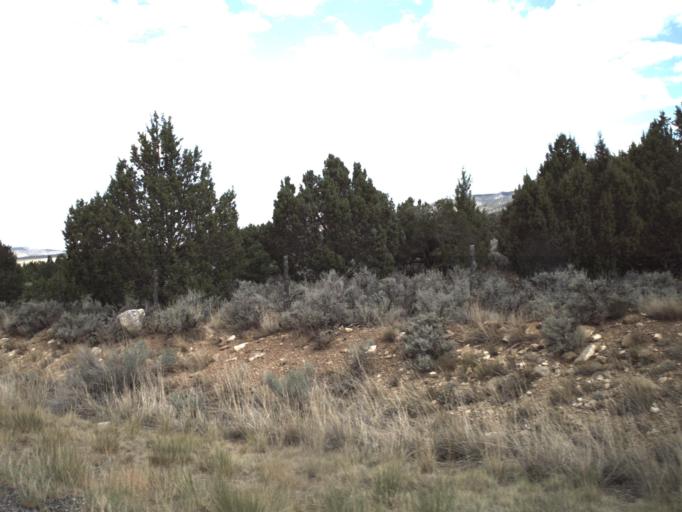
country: US
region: Utah
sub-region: Sanpete County
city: Gunnison
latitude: 39.1995
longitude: -112.0843
